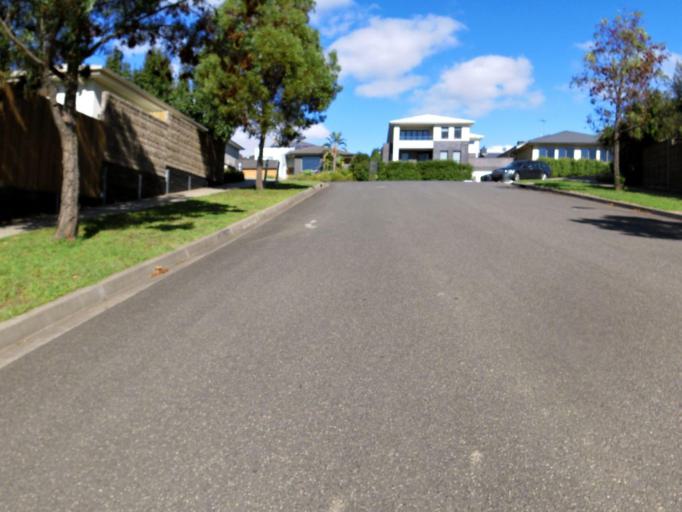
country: AU
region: Victoria
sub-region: Greater Geelong
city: Wandana Heights
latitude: -38.1615
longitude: 144.3033
